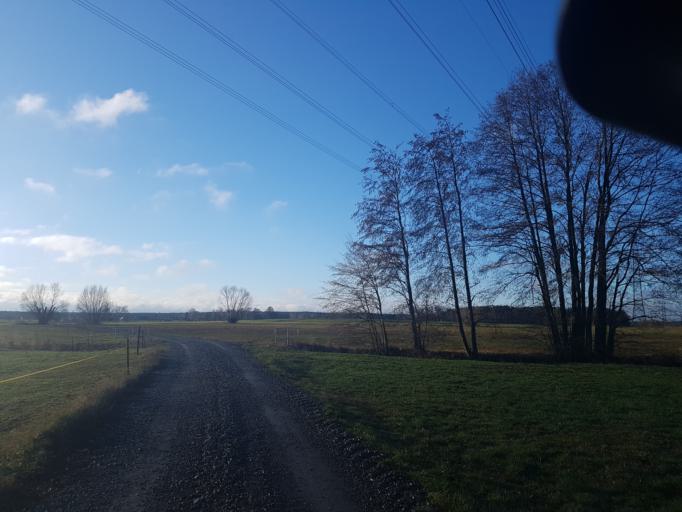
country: DE
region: Brandenburg
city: Schonborn
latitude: 51.5552
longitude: 13.4724
